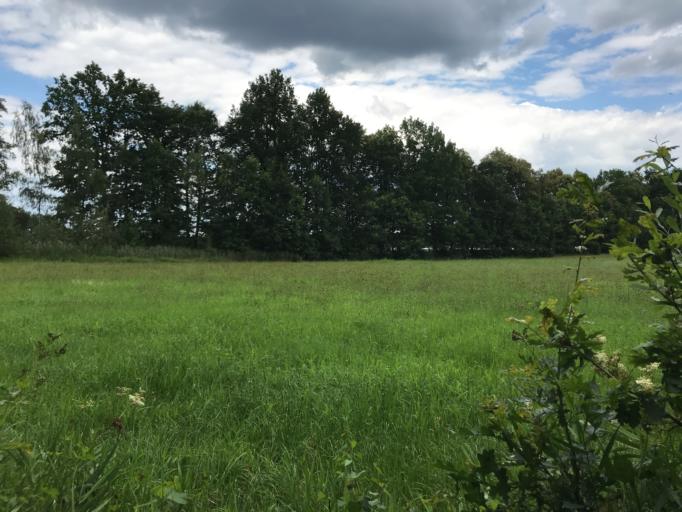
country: CZ
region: Jihocesky
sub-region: Okres Jindrichuv Hradec
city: Lomnice nad Luznici
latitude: 49.0916
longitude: 14.7087
